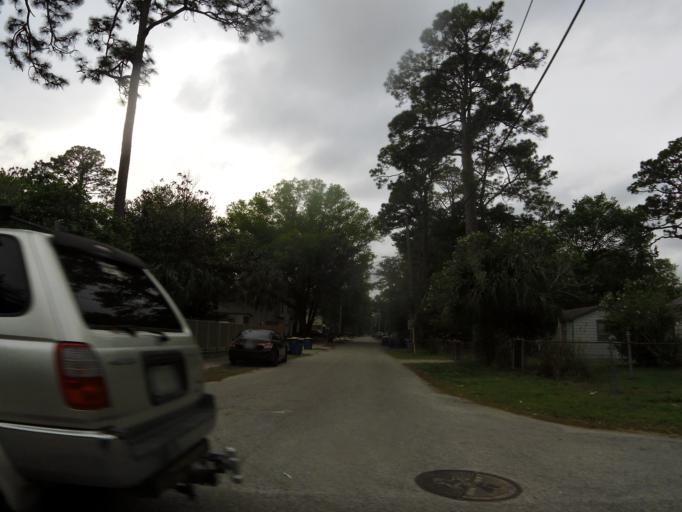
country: US
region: Florida
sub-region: Duval County
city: Jacksonville
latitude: 30.3174
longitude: -81.5660
